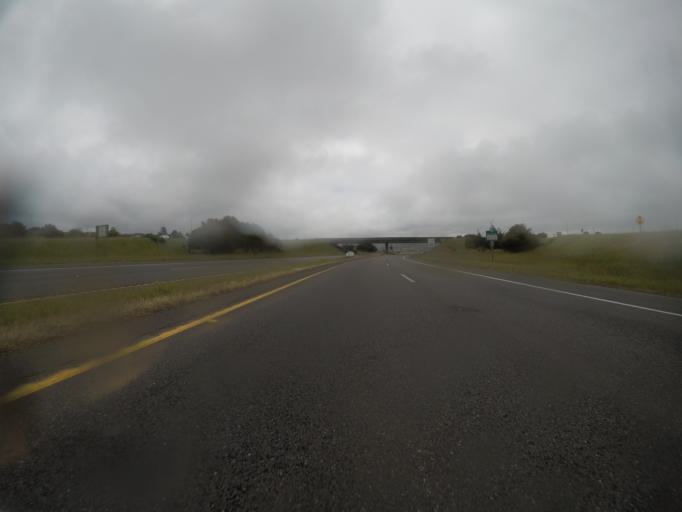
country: US
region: California
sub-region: Humboldt County
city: Bayview
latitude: 40.7592
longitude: -124.1895
